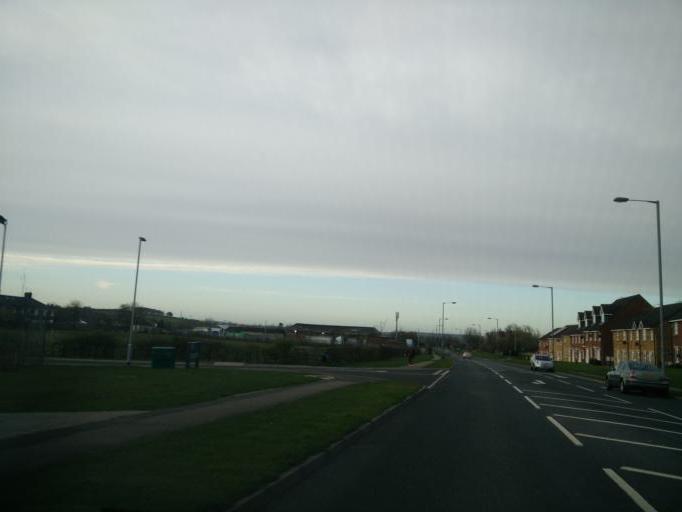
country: GB
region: England
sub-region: County Durham
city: Crook
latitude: 54.7114
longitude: -1.7518
